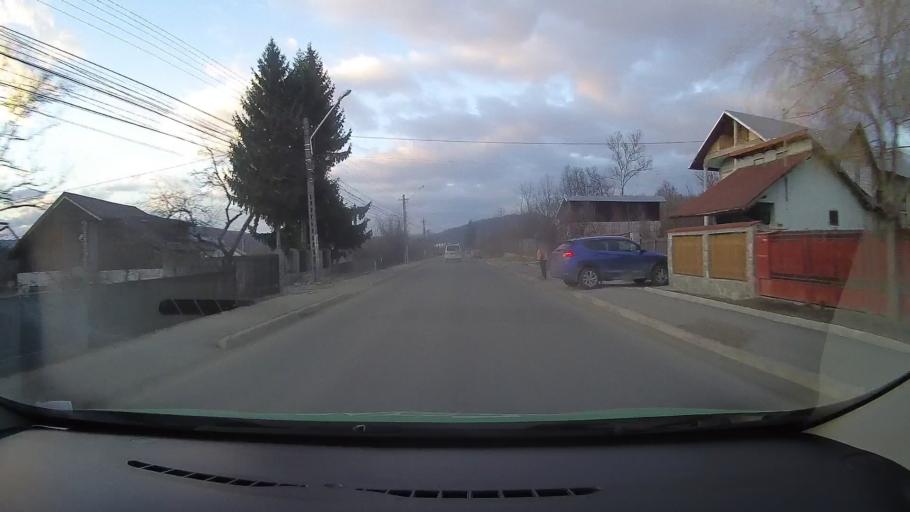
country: RO
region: Dambovita
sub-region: Municipiul Moreni
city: Moreni
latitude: 44.9987
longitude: 25.6477
